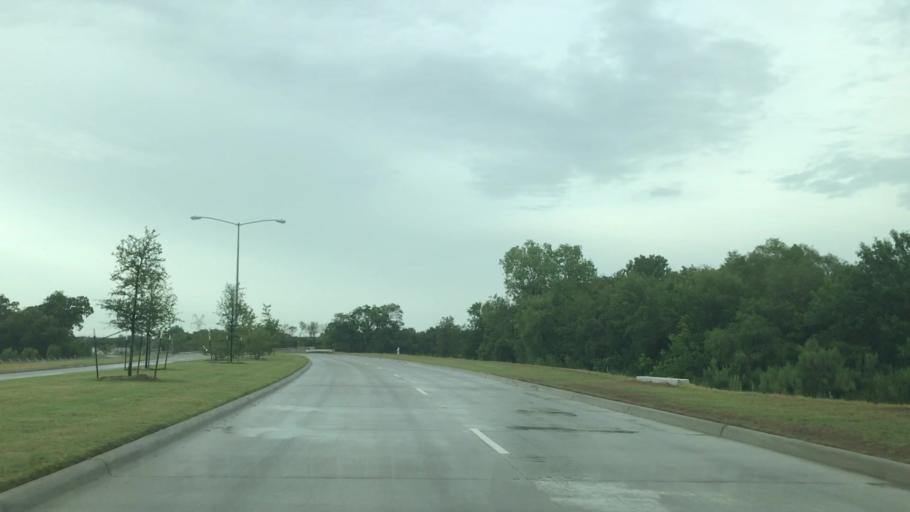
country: US
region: Texas
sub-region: Denton County
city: Lewisville
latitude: 33.0527
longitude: -96.9809
